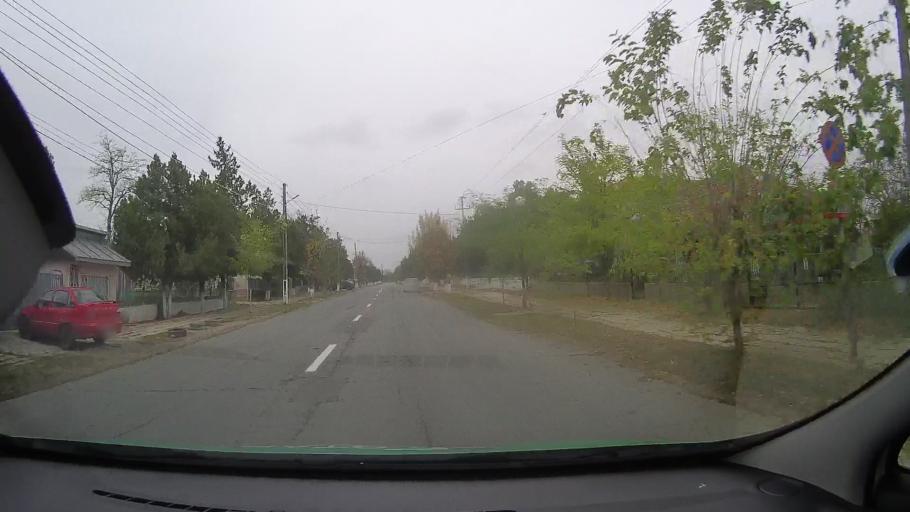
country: RO
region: Constanta
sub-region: Comuna Pantelimon
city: Pantelimon
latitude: 44.5446
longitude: 28.3290
